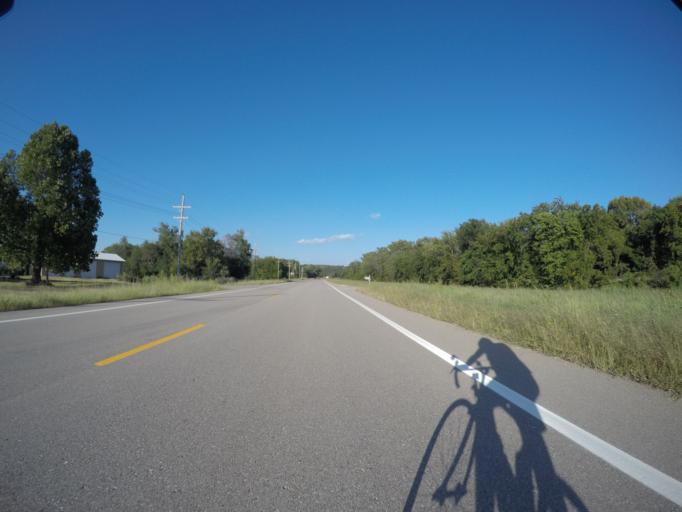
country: US
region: Kansas
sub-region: Riley County
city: Manhattan
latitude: 39.1550
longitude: -96.6359
